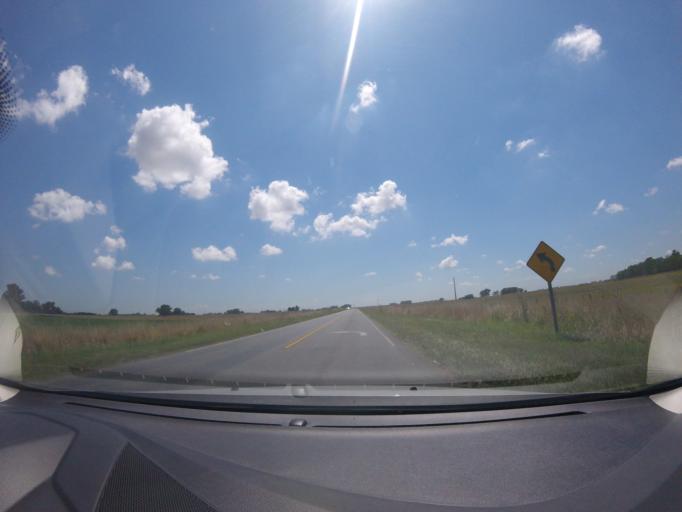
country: AR
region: Buenos Aires
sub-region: Partido de Rauch
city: Rauch
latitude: -36.7424
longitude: -59.0634
